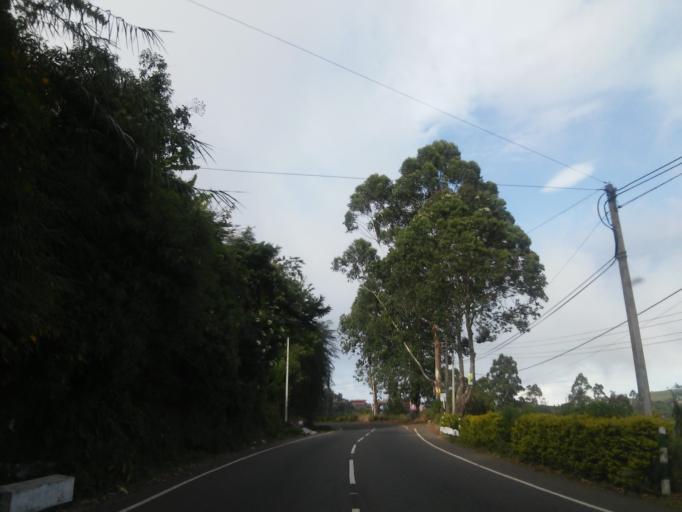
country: LK
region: Uva
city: Haputale
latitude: 6.7737
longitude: 80.9626
